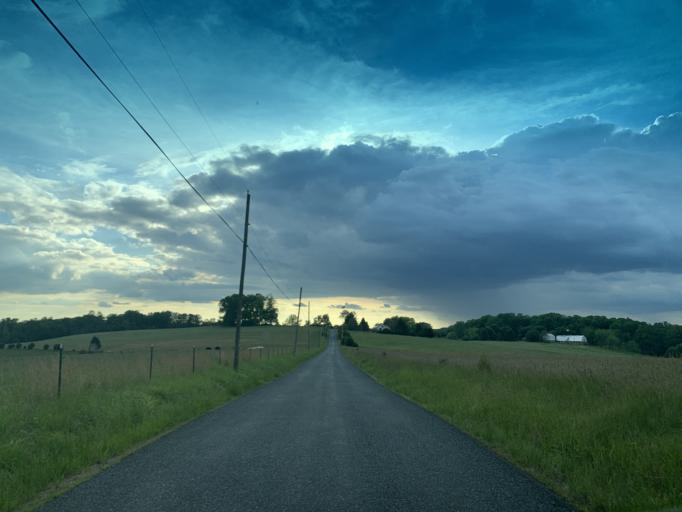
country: US
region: Pennsylvania
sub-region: York County
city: Susquehanna Trails
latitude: 39.6721
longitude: -76.2617
